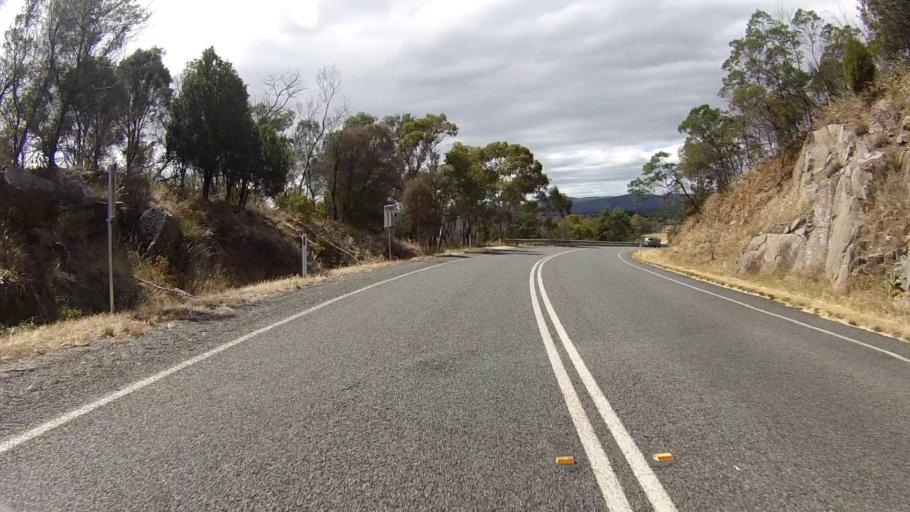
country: AU
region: Tasmania
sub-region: Sorell
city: Sorell
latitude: -42.6068
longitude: 147.6812
